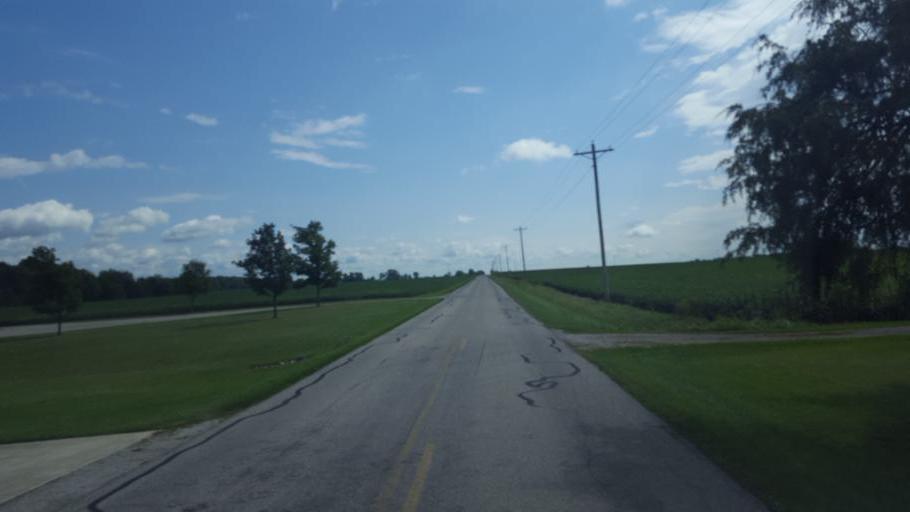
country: US
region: Ohio
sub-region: Seneca County
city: Tiffin
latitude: 41.0666
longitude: -83.0608
